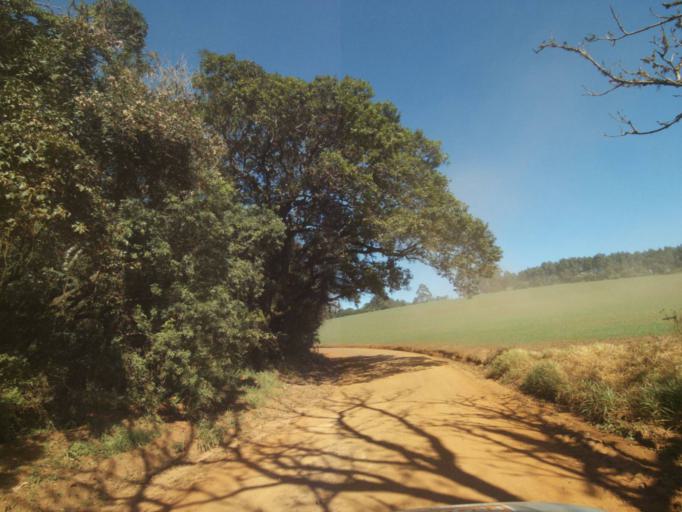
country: BR
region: Parana
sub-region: Tibagi
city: Tibagi
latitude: -24.5676
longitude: -50.6273
